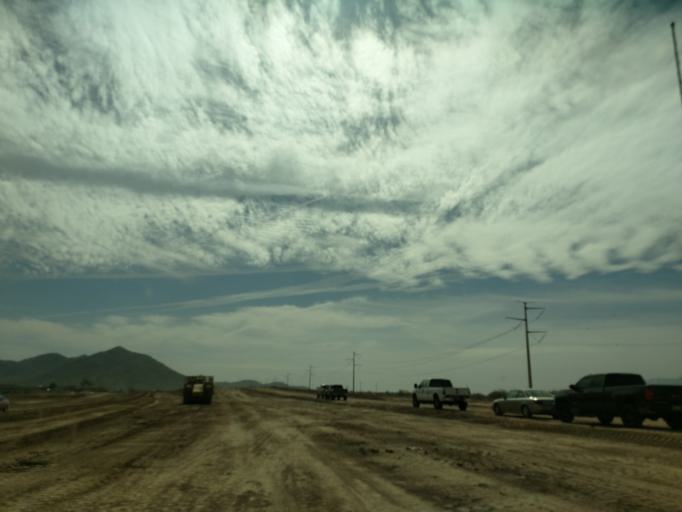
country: US
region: Arizona
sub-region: Maricopa County
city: Laveen
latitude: 33.3378
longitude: -112.1803
